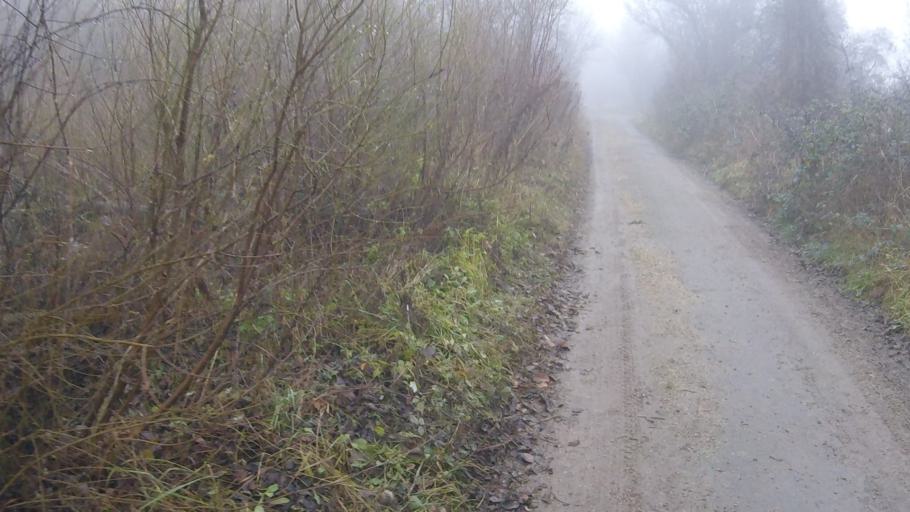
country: HU
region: Pest
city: Budakeszi
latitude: 47.5383
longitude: 18.9351
